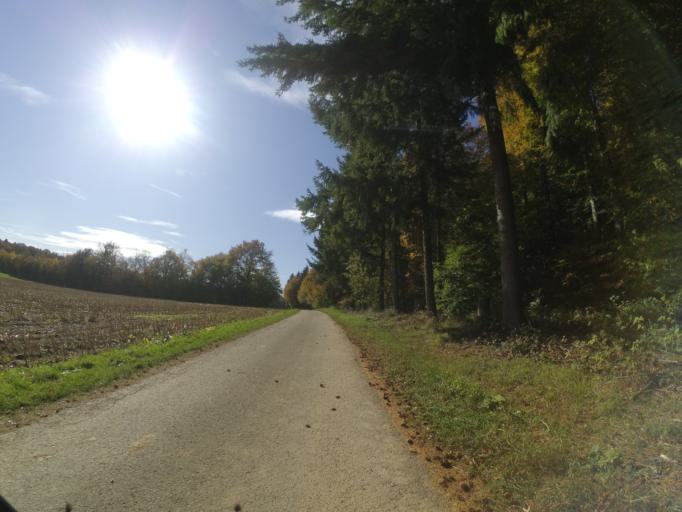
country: DE
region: Baden-Wuerttemberg
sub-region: Tuebingen Region
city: Weidenstetten
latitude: 48.5442
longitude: 9.9780
